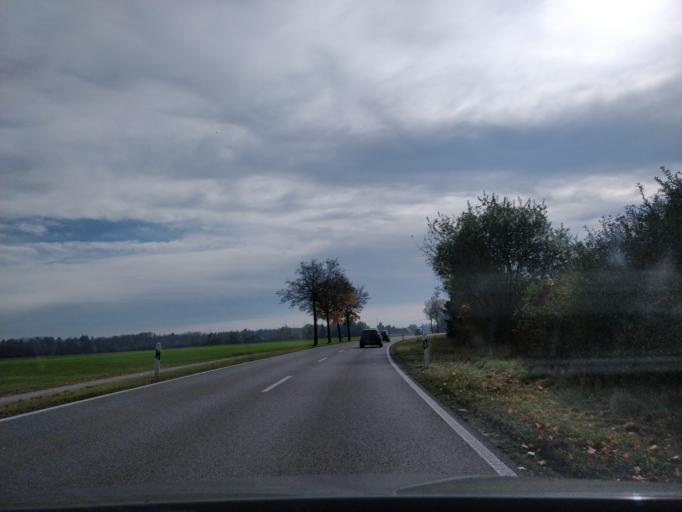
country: DE
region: Bavaria
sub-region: Swabia
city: Konigsbrunn
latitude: 48.2571
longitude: 10.9050
